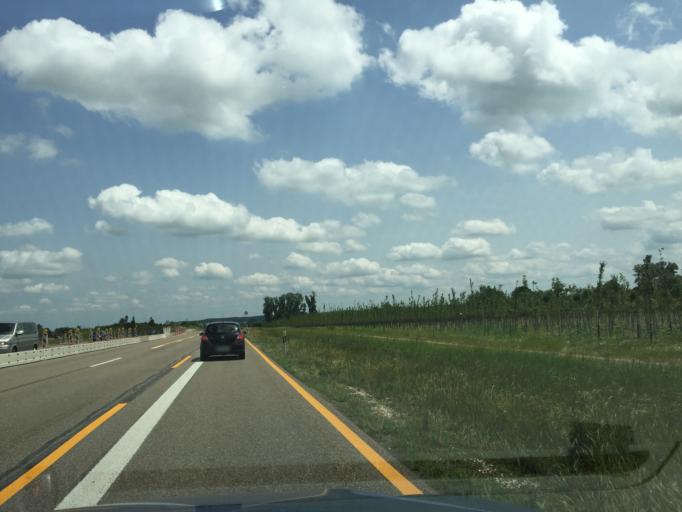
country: DE
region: Bavaria
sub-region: Swabia
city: Bubesheim
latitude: 48.4289
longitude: 10.2407
